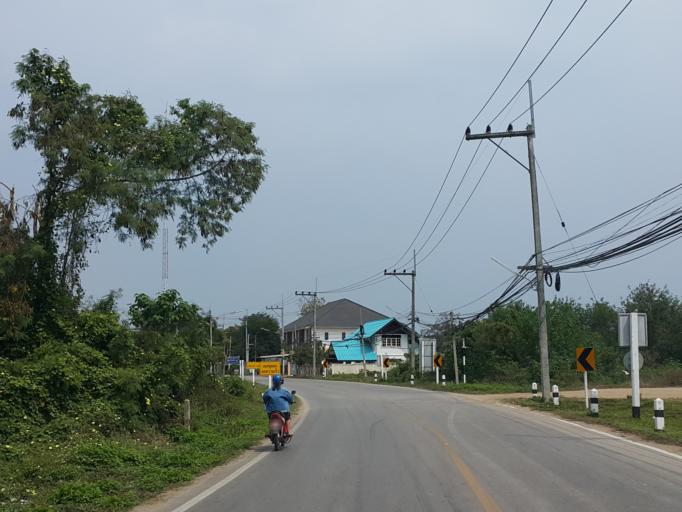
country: TH
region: Lampang
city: Ko Kha
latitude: 18.1798
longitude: 99.3944
